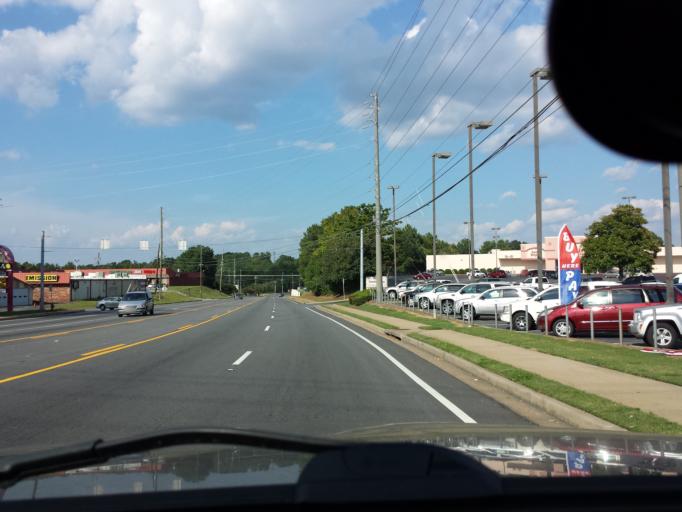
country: US
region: Georgia
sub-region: Cobb County
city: Smyrna
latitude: 33.9053
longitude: -84.4892
